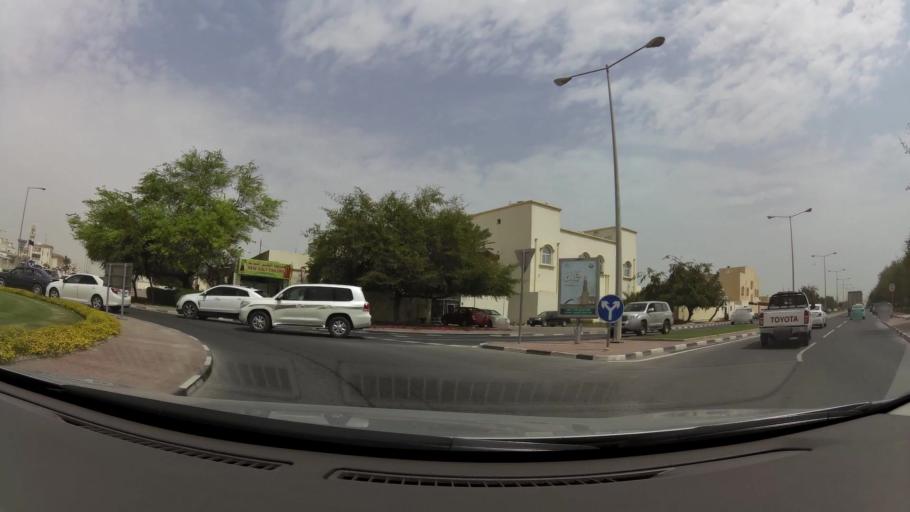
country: QA
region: Baladiyat ad Dawhah
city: Doha
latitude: 25.3141
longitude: 51.4788
